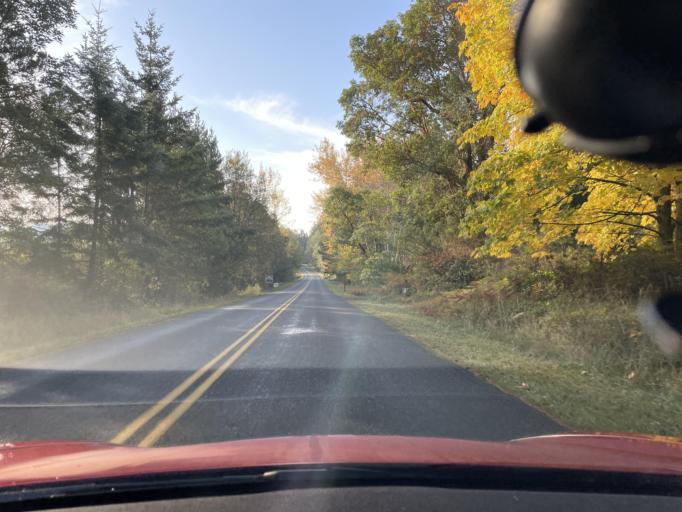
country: US
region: Washington
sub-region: San Juan County
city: Friday Harbor
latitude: 48.5619
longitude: -123.1647
